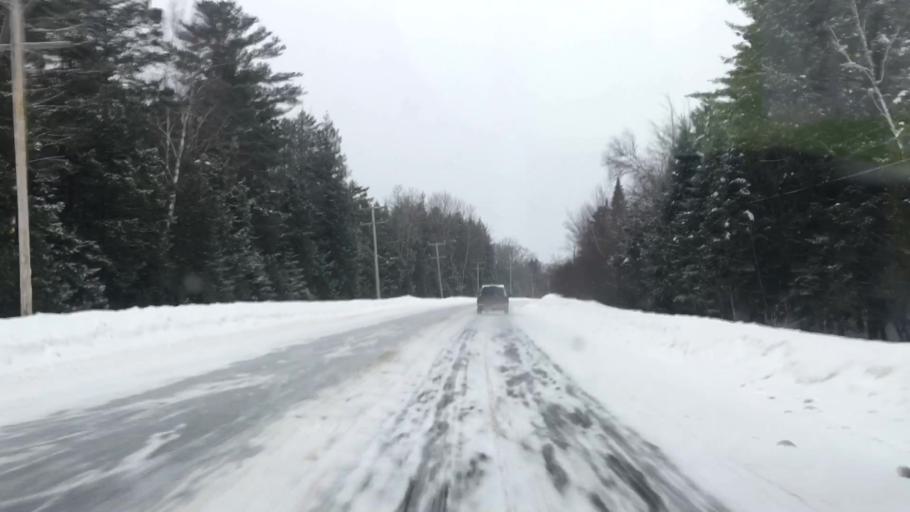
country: US
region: Maine
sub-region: Penobscot County
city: Medway
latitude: 45.5954
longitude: -68.4816
